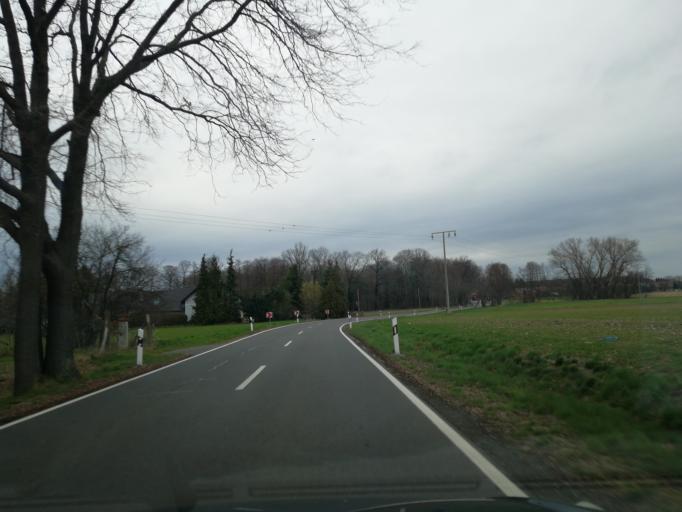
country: DE
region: Brandenburg
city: Vetschau
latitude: 51.7552
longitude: 14.0537
